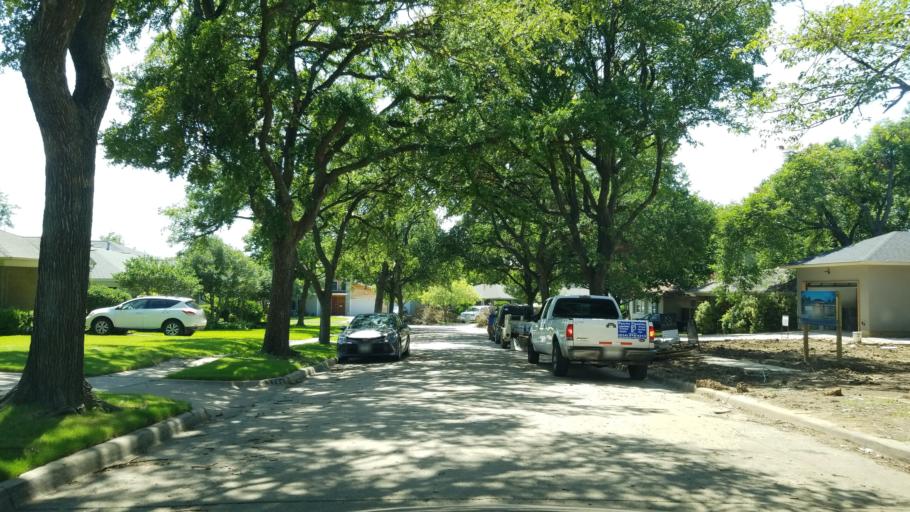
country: US
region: Texas
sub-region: Dallas County
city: University Park
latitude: 32.8794
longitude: -96.8532
